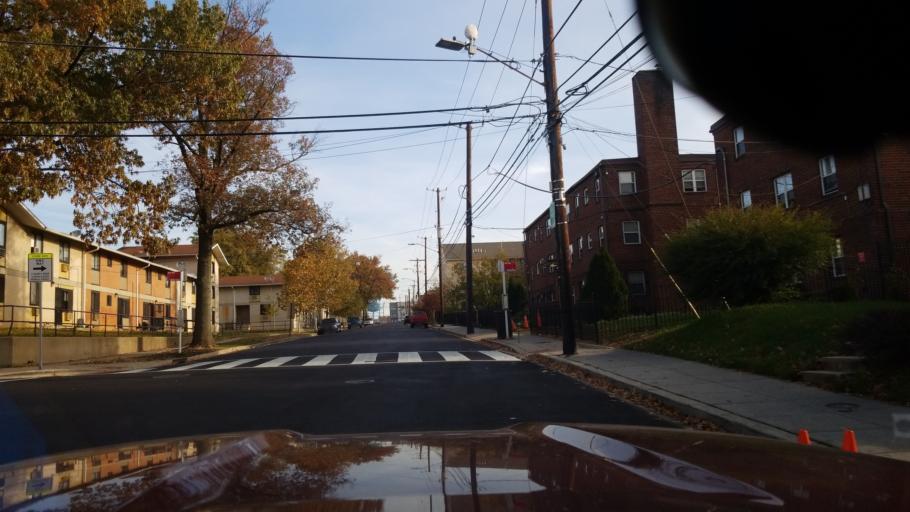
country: US
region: Maryland
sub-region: Prince George's County
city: Hillcrest Heights
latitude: 38.8553
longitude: -76.9735
